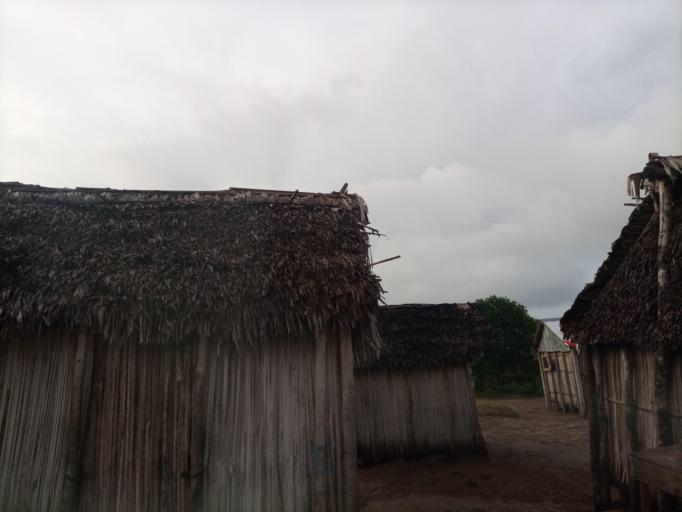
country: MG
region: Anosy
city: Fort Dauphin
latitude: -24.7035
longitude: 47.1777
